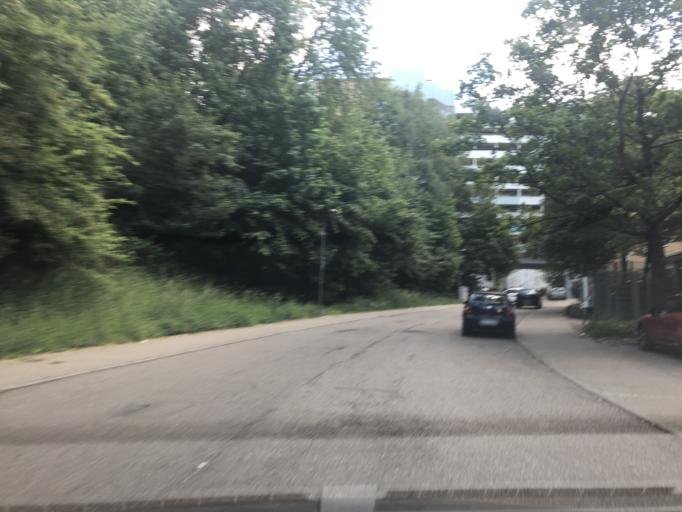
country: DE
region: Baden-Wuerttemberg
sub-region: Karlsruhe Region
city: Leimen
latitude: 49.3637
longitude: 8.7055
